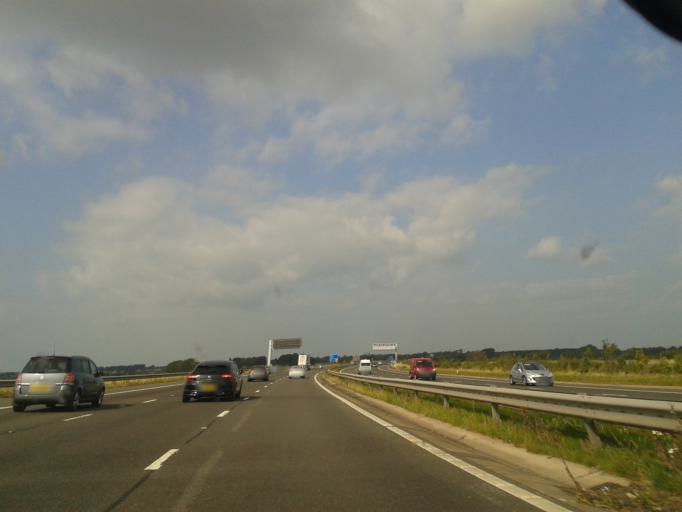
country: GB
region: Scotland
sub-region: Dumfries and Galloway
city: Gretna
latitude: 54.9848
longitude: -3.0333
